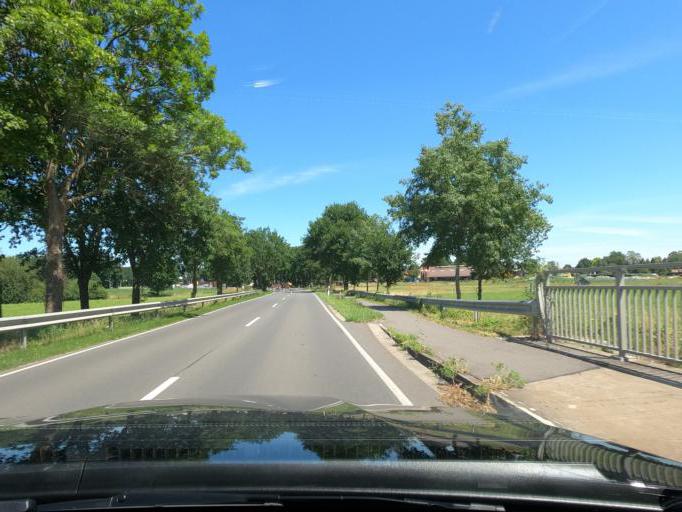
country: DE
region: Lower Saxony
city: Eicklingen
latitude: 52.5457
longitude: 10.1714
